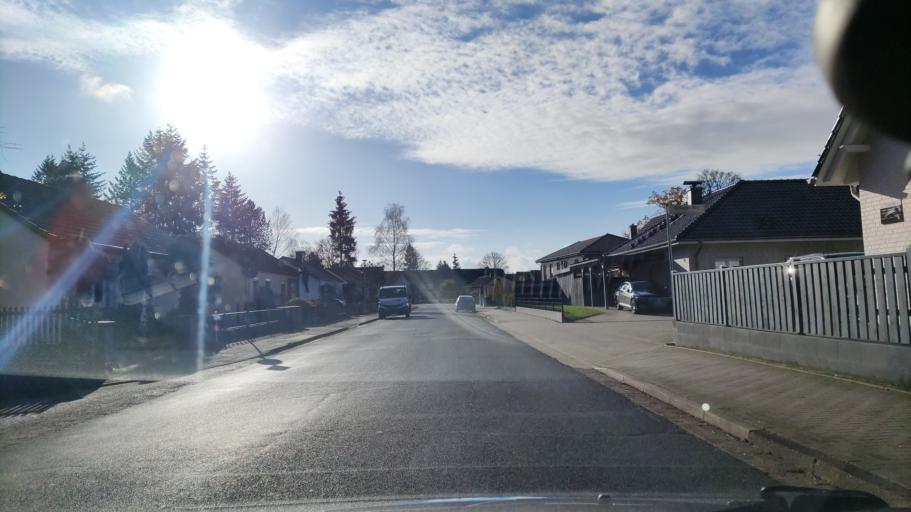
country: DE
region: Lower Saxony
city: Soltau
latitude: 52.9894
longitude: 9.8535
